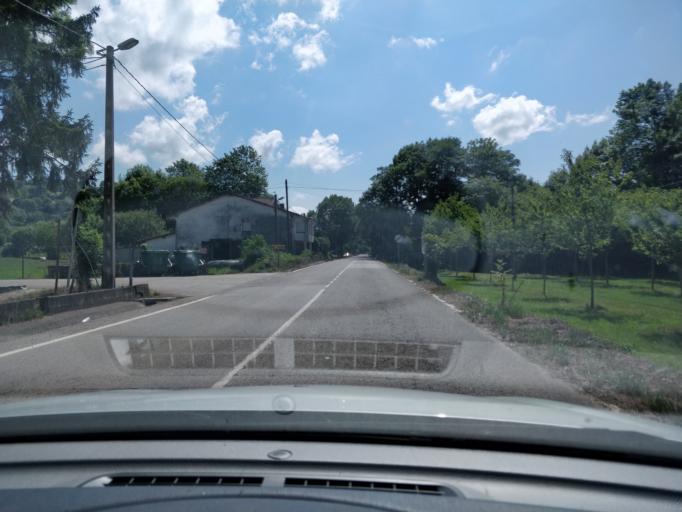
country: ES
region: Cantabria
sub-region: Provincia de Cantabria
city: Corvera
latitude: 43.2687
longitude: -3.9226
